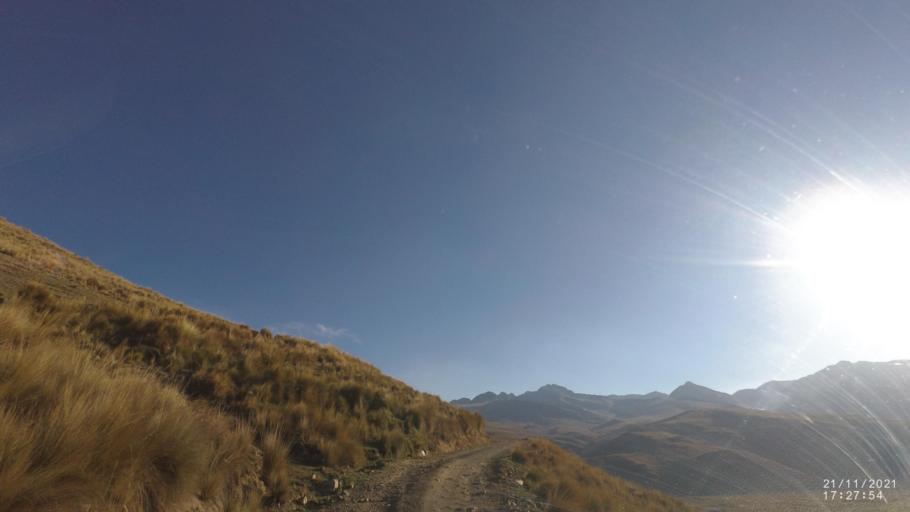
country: BO
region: Cochabamba
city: Cochabamba
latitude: -17.1746
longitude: -66.2593
